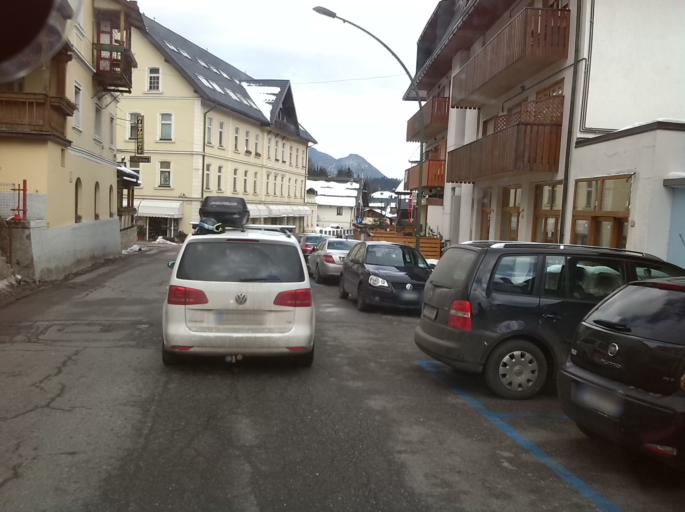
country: IT
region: Friuli Venezia Giulia
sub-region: Provincia di Udine
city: Tarvisio
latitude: 46.5044
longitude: 13.5796
